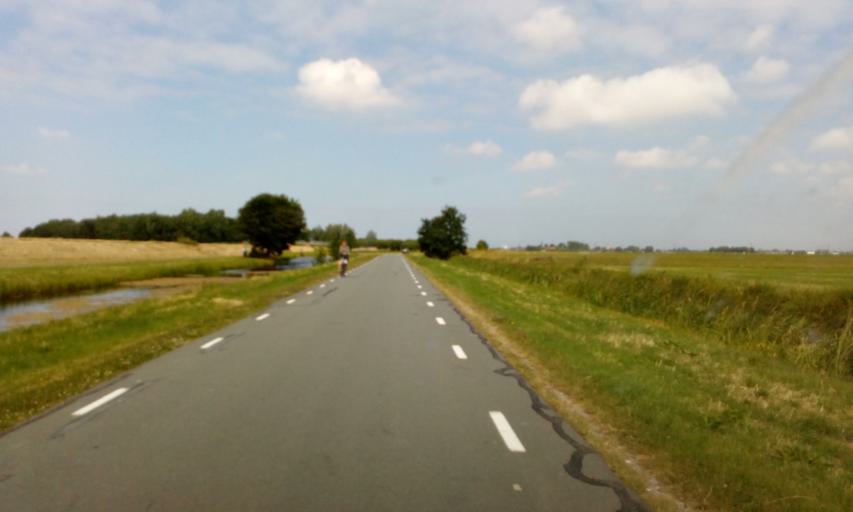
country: NL
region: South Holland
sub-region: Gemeente Delft
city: Delft
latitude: 51.9778
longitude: 4.3061
